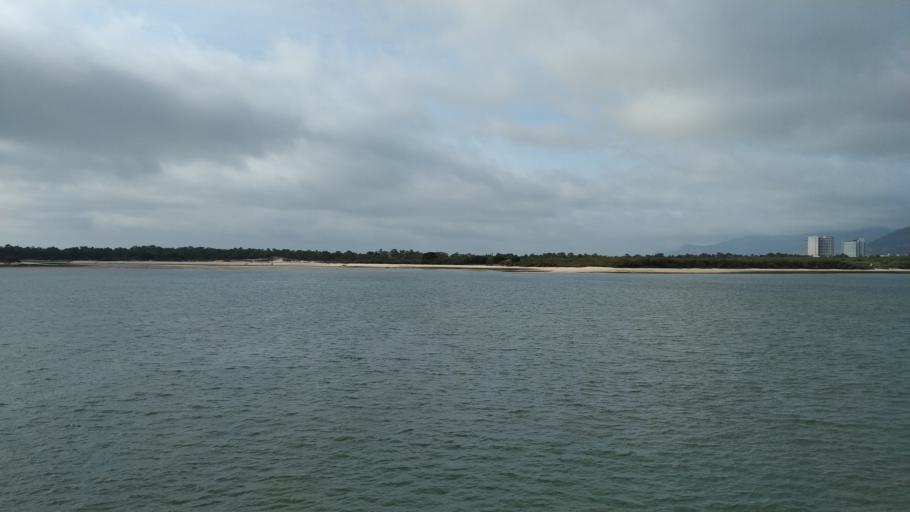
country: PT
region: Setubal
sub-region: Setubal
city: Setubal
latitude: 38.4928
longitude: -8.8832
